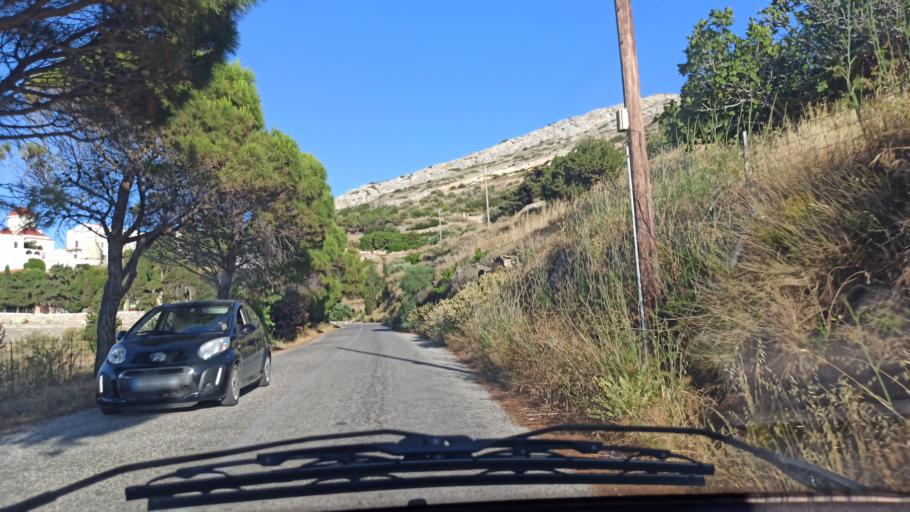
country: GR
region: South Aegean
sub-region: Nomos Kykladon
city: Ano Syros
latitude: 37.4434
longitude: 24.9174
